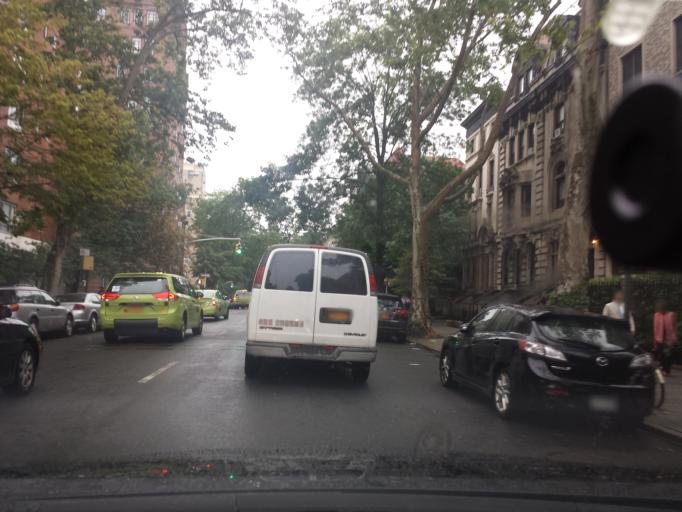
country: US
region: New York
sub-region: Kings County
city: Brooklyn
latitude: 40.6717
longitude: -73.9743
